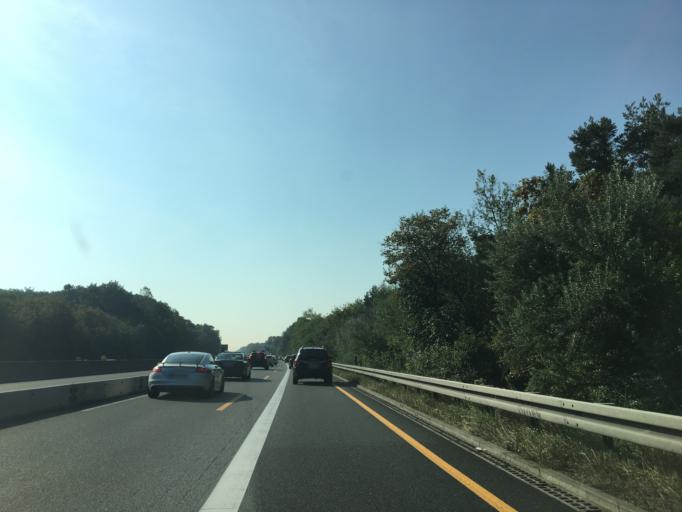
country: DE
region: Hesse
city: Lorsch
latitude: 49.6512
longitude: 8.5518
